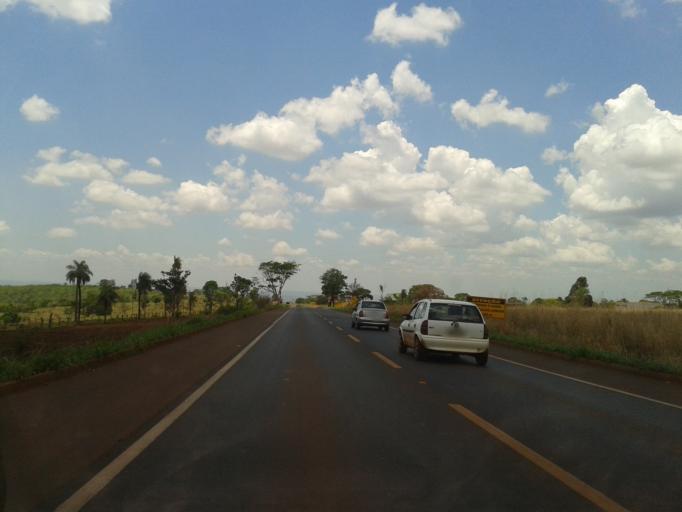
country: BR
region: Goias
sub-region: Itumbiara
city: Itumbiara
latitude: -18.3915
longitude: -49.3353
